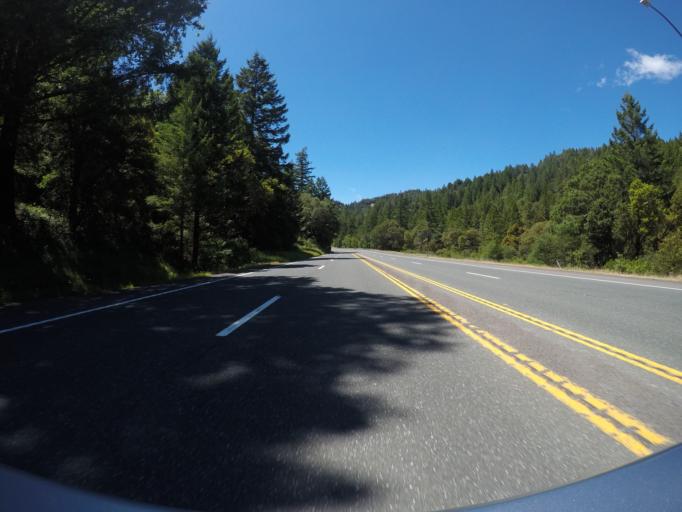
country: US
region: California
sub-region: Mendocino County
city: Laytonville
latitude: 39.8277
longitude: -123.5970
